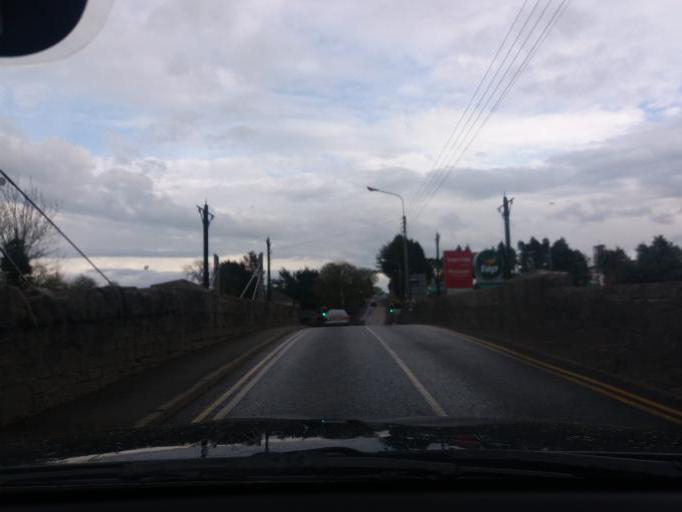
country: IE
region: Ulster
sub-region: An Cabhan
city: Ballyconnell
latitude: 54.1159
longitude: -7.5835
